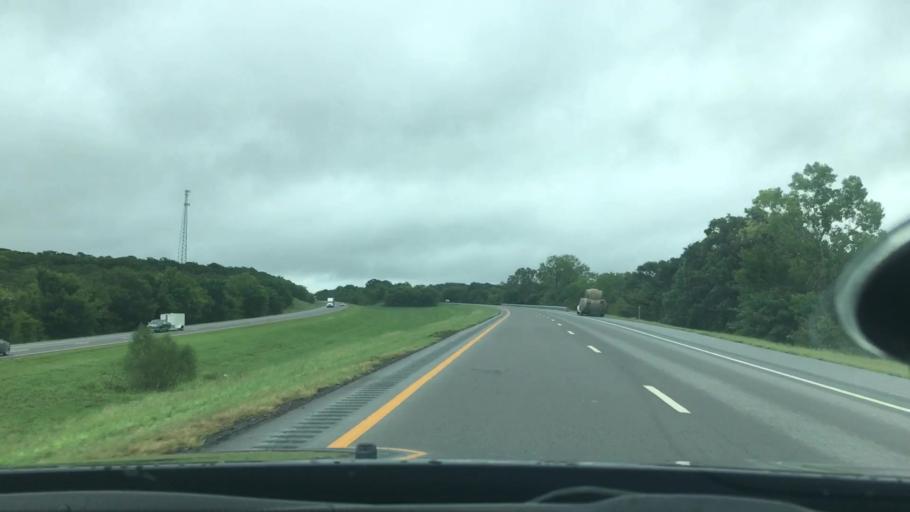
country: US
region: Oklahoma
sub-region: Okmulgee County
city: Henryetta
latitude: 35.4338
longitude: -95.8147
